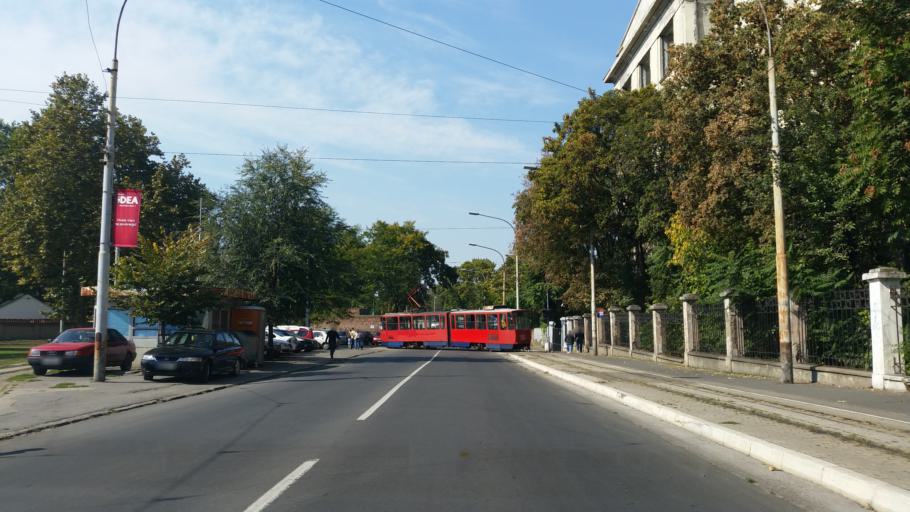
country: RS
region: Central Serbia
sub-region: Belgrade
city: Stari Grad
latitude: 44.8268
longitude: 20.4537
